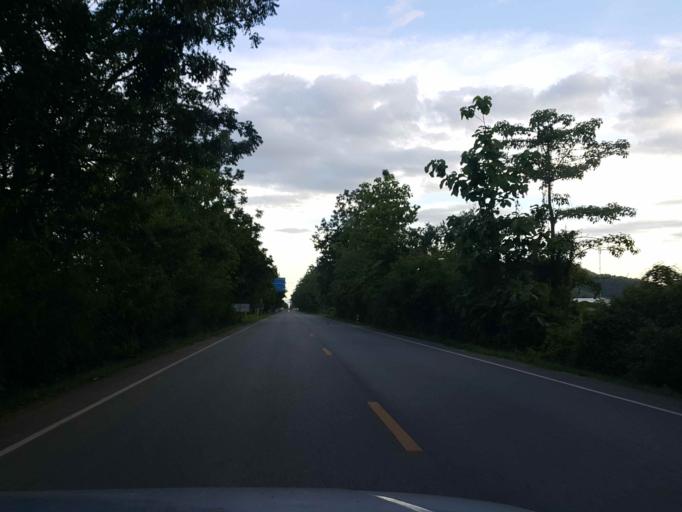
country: TH
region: Sukhothai
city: Sawankhalok
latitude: 17.3144
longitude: 99.7344
